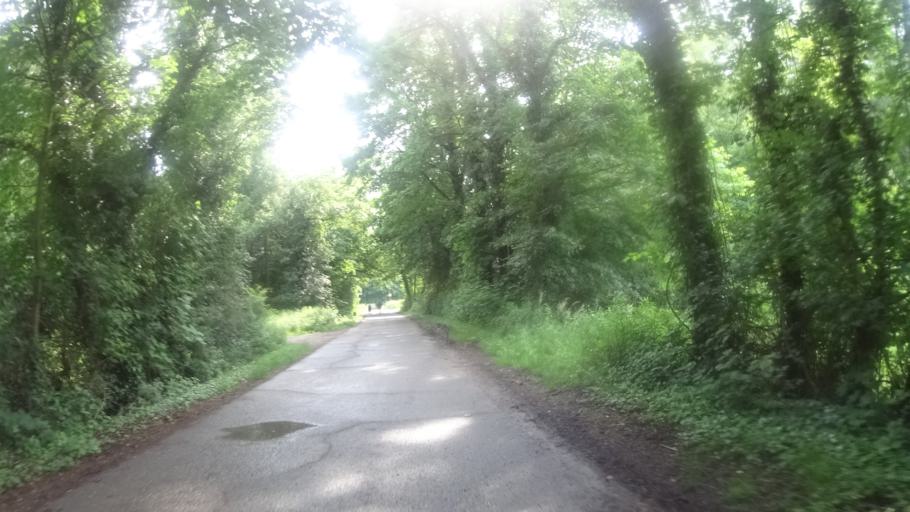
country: DE
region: Baden-Wuerttemberg
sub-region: Karlsruhe Region
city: Iffezheim
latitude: 48.8189
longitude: 8.1268
